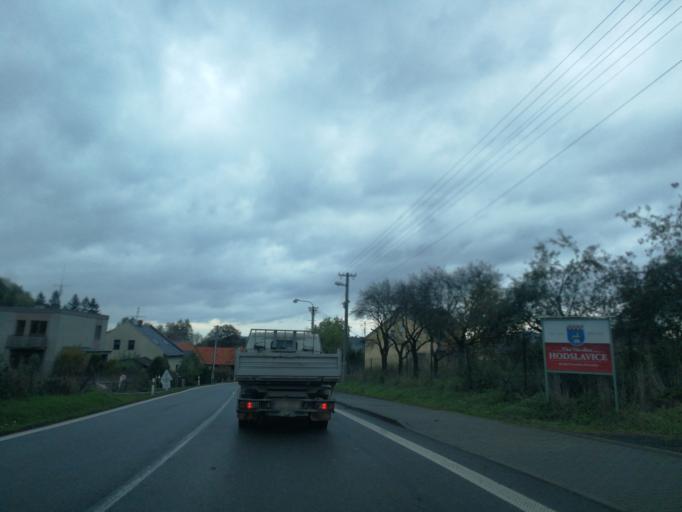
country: CZ
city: Hodslavice
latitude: 49.5323
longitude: 18.0188
